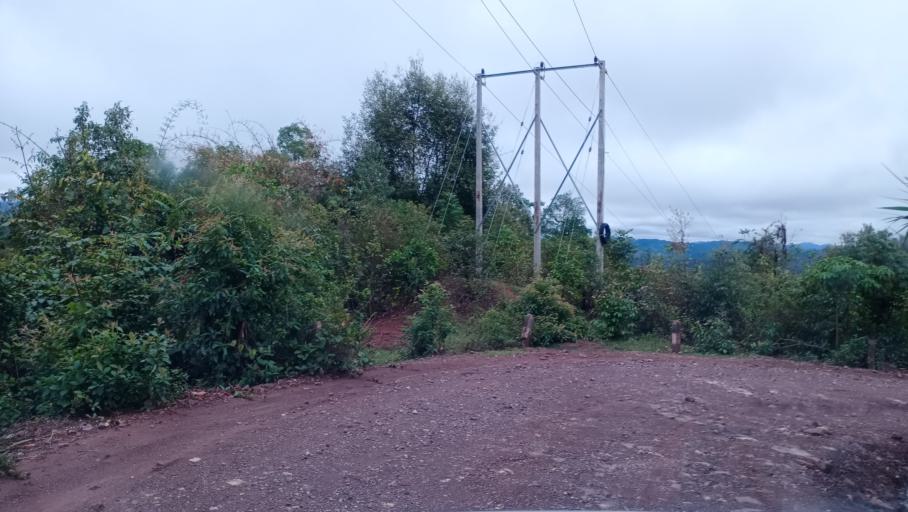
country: LA
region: Phongsali
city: Phongsali
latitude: 21.3409
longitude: 102.0768
